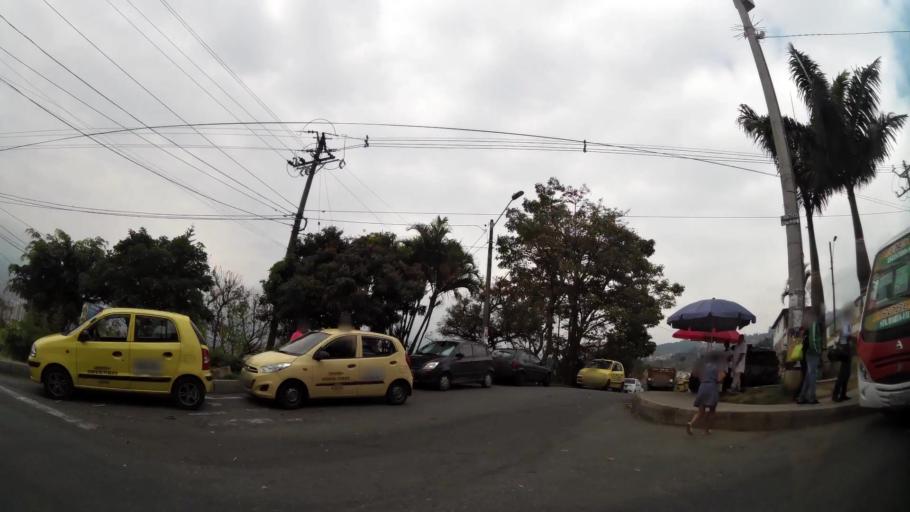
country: CO
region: Antioquia
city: Medellin
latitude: 6.2873
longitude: -75.5993
